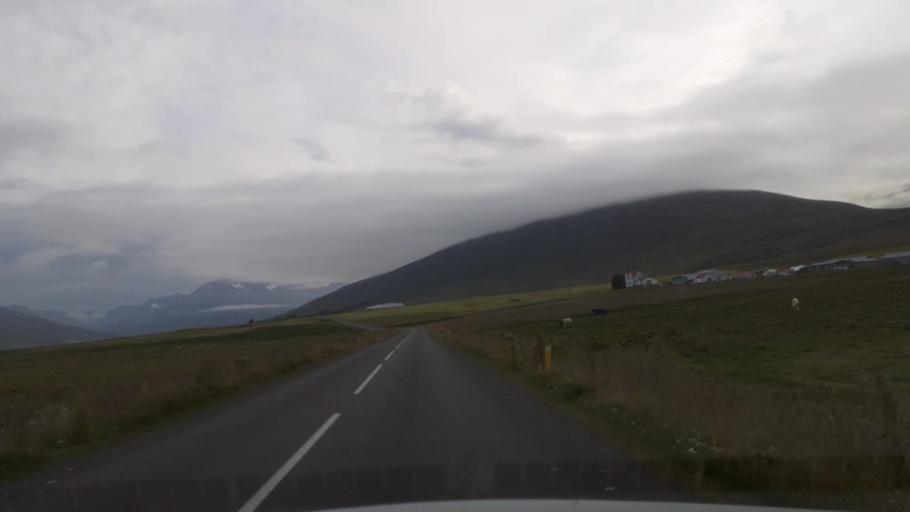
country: IS
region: Northeast
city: Dalvik
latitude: 65.9604
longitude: -18.5437
